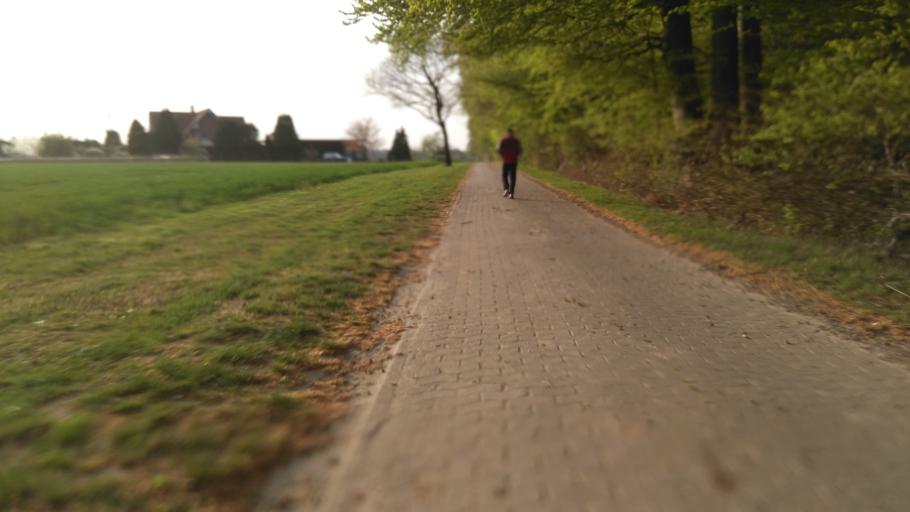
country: DE
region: Lower Saxony
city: Apensen
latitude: 53.4654
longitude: 9.6400
